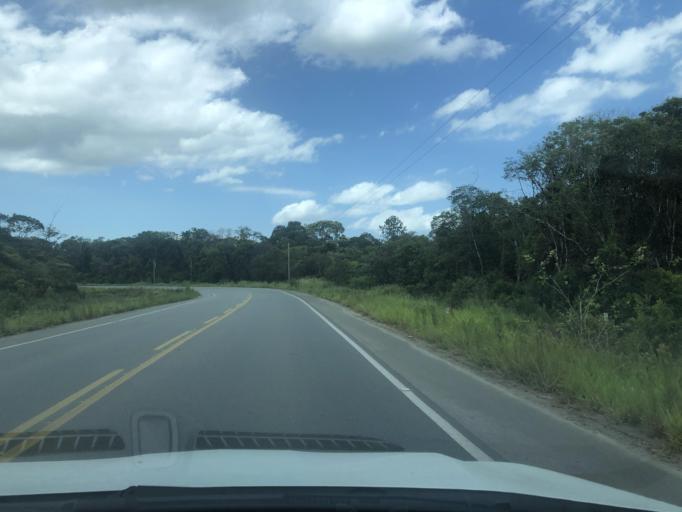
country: BR
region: Santa Catarina
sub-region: Joinville
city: Joinville
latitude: -26.4022
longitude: -48.7572
